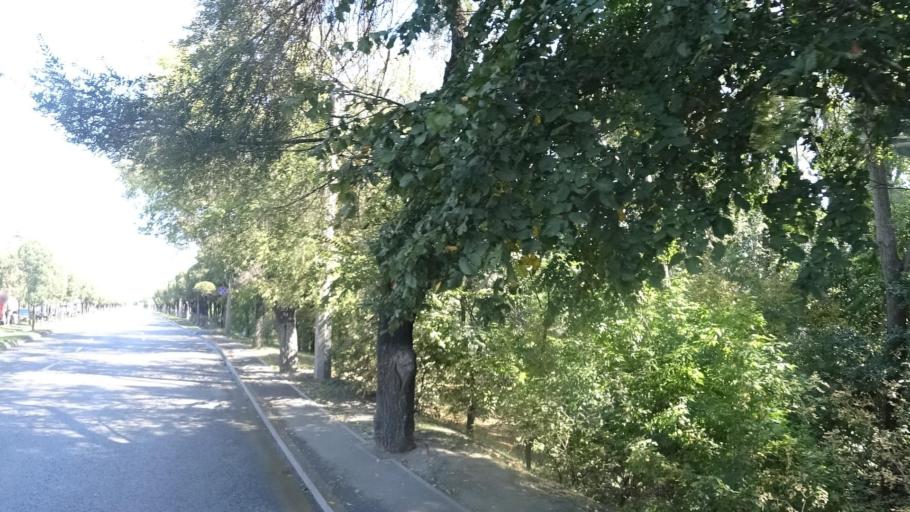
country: KZ
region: Almaty Oblysy
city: Pervomayskiy
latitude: 43.3224
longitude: 76.9733
